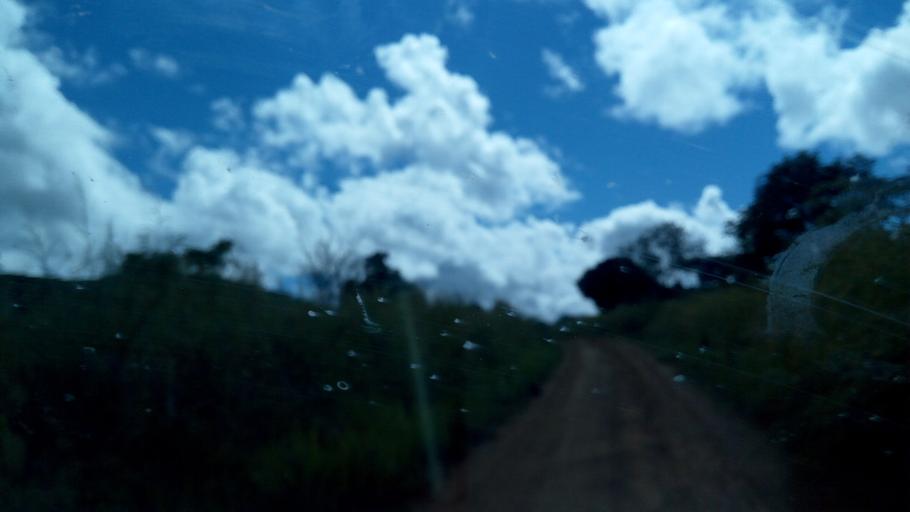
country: ZM
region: Northern
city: Kaputa
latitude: -8.2215
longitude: 29.0536
